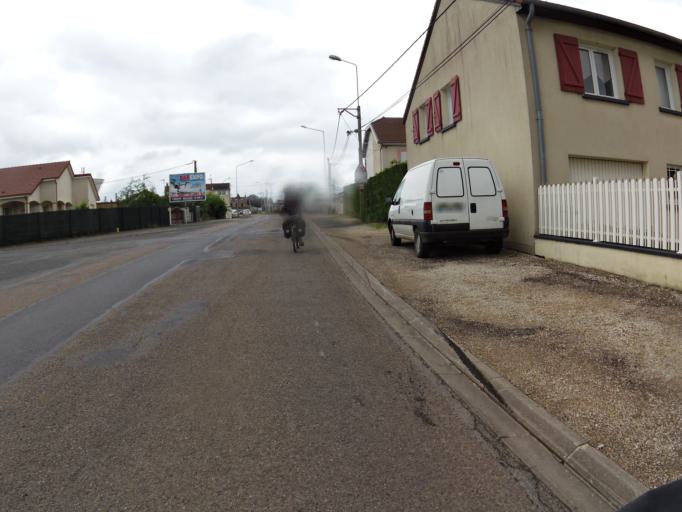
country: FR
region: Champagne-Ardenne
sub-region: Departement de la Haute-Marne
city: Saint-Dizier
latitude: 48.6451
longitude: 4.9346
